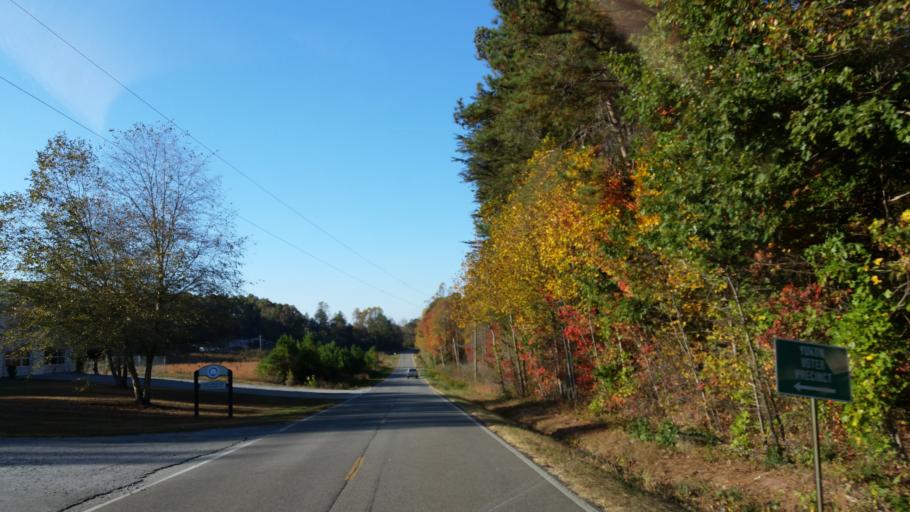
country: US
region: Georgia
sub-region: Gilmer County
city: Ellijay
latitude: 34.5968
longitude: -84.4605
